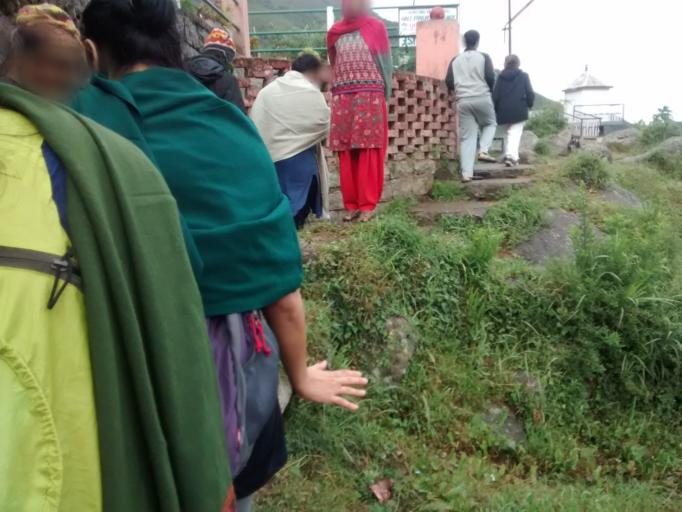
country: IN
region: Himachal Pradesh
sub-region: Kangra
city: Dharmsala
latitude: 32.2480
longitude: 76.3302
